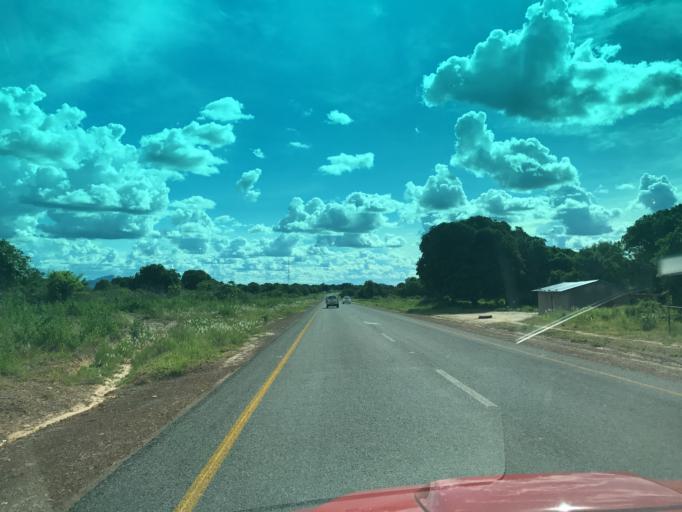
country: MZ
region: Nampula
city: Nampula
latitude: -15.0009
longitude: 39.0177
